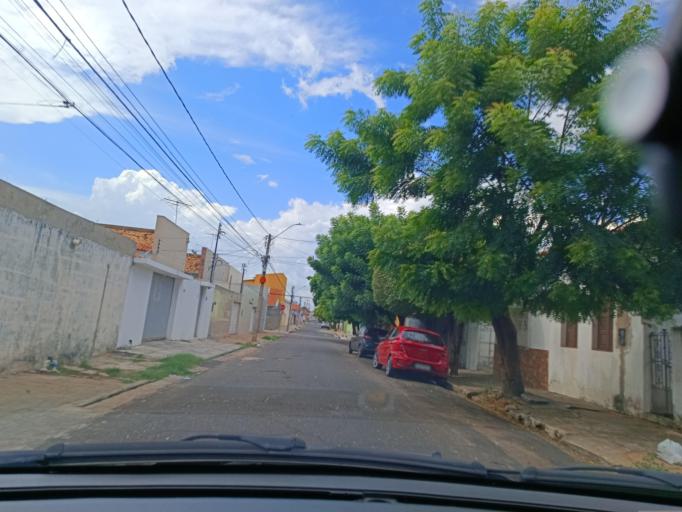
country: BR
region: Piaui
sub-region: Teresina
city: Teresina
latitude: -5.0835
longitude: -42.8151
